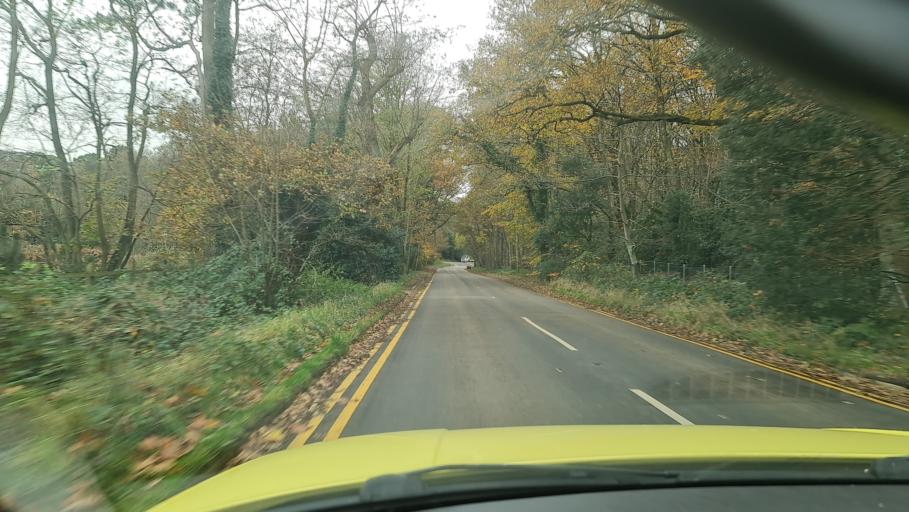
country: GB
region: England
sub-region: Hampshire
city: Aldershot
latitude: 51.2535
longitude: -0.7827
